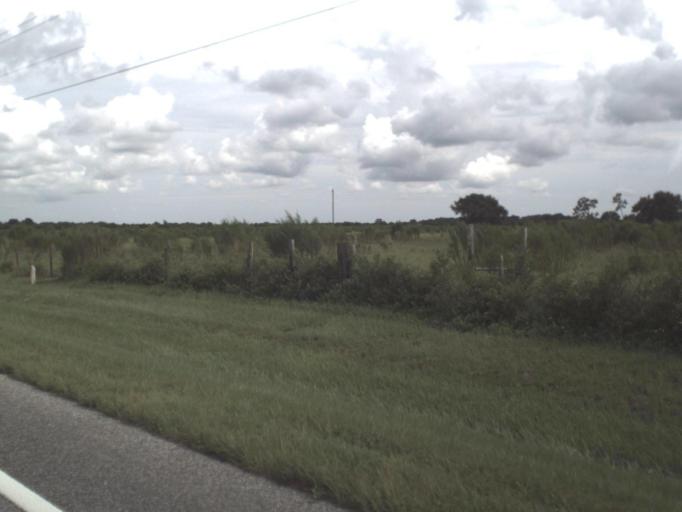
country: US
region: Florida
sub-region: DeSoto County
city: Nocatee
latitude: 27.2014
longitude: -81.9427
